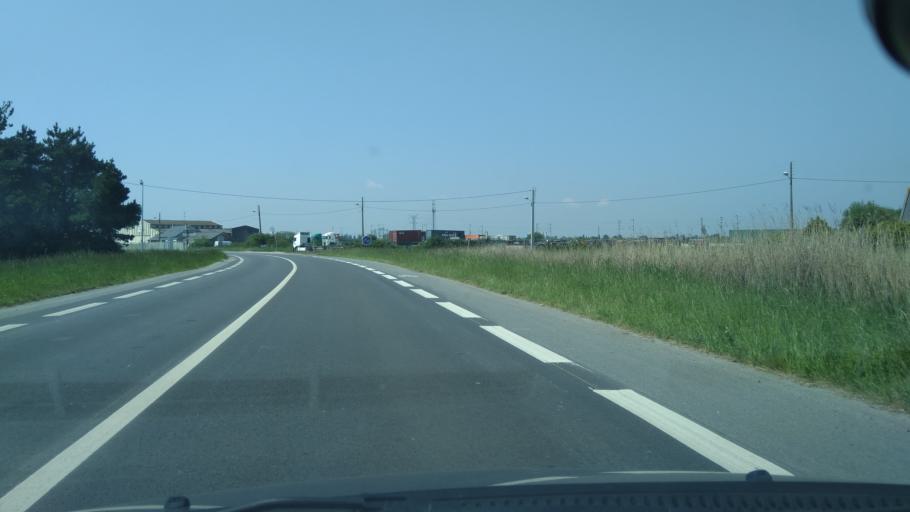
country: FR
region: Pays de la Loire
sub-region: Departement de la Loire-Atlantique
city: Montoir-de-Bretagne
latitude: 47.3176
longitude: -2.1654
